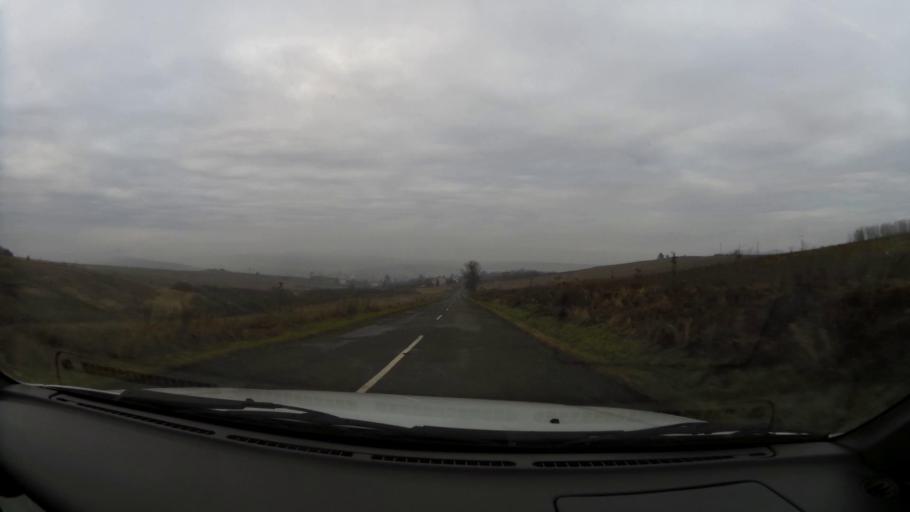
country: HU
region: Borsod-Abauj-Zemplen
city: Rudabanya
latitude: 48.3976
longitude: 20.6283
